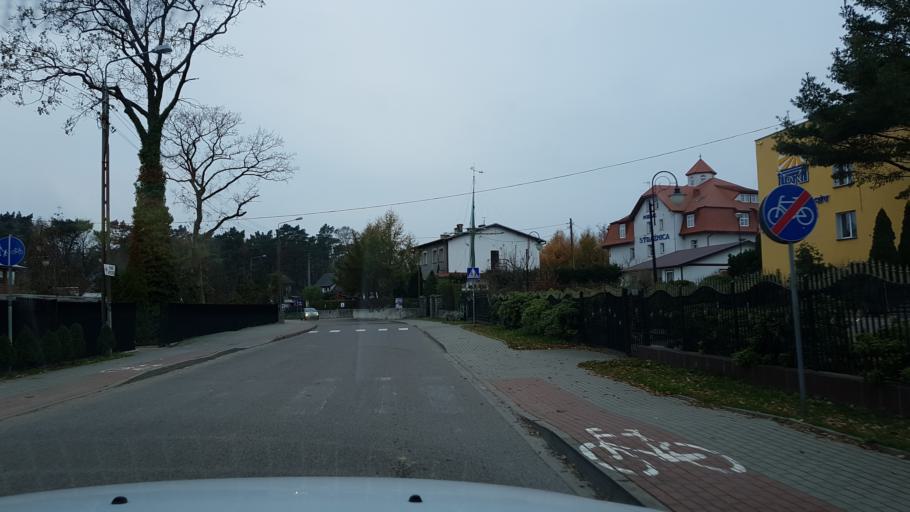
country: PL
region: West Pomeranian Voivodeship
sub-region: Powiat slawienski
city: Darlowo
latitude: 54.5385
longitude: 16.5313
